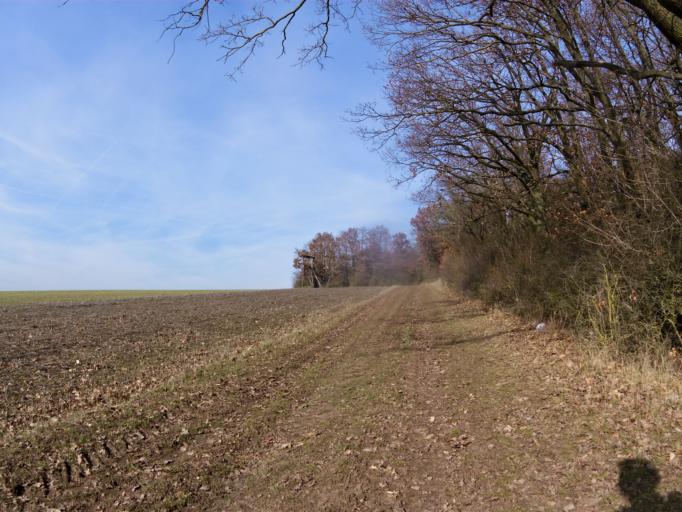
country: DE
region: Bavaria
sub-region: Regierungsbezirk Unterfranken
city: Kurnach
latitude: 49.8271
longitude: 10.0372
